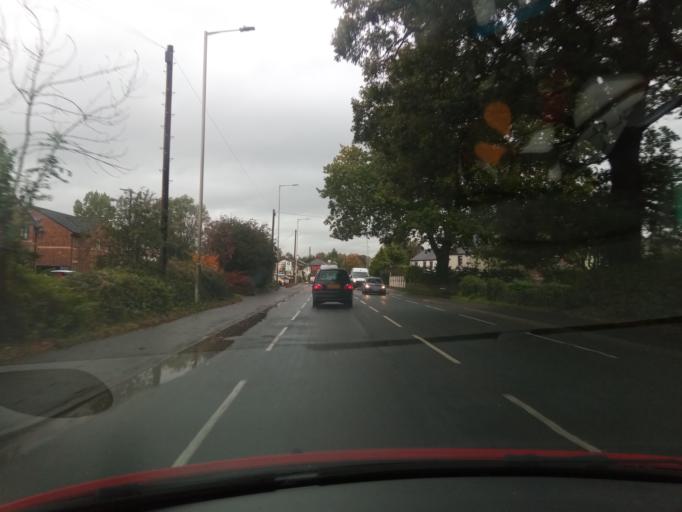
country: GB
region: England
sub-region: Lancashire
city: Catterall
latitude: 53.8561
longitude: -2.7449
